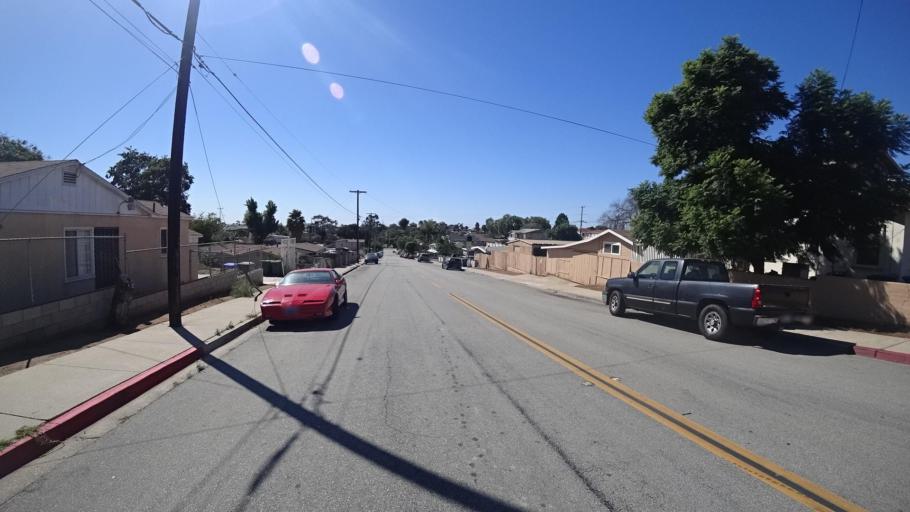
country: US
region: California
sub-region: San Diego County
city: National City
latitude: 32.6700
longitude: -117.0731
